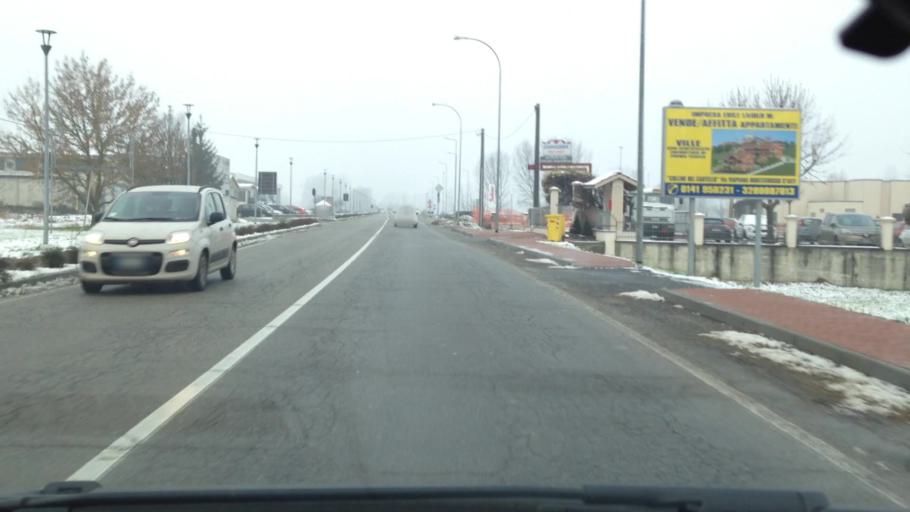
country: IT
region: Piedmont
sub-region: Provincia di Asti
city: Montegrosso
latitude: 44.8200
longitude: 8.2323
